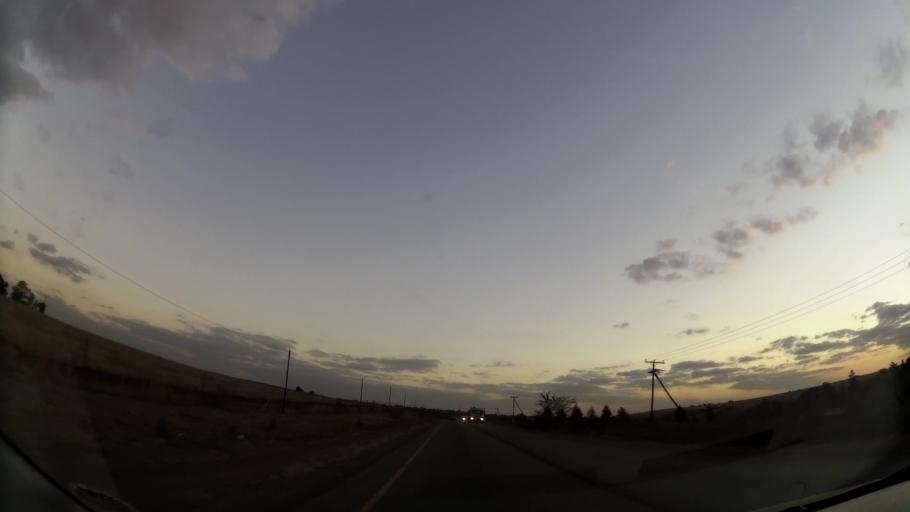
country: ZA
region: Gauteng
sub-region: West Rand District Municipality
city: Krugersdorp
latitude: -26.0589
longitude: 27.7035
